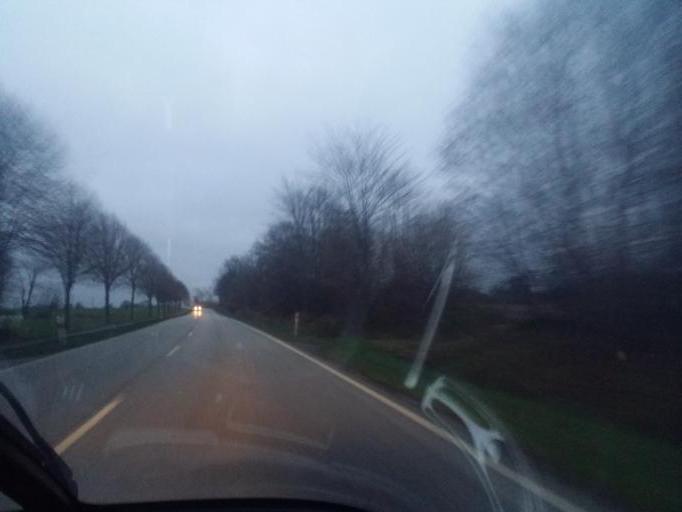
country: DE
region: Schleswig-Holstein
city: Gokels
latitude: 54.1166
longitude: 9.4526
